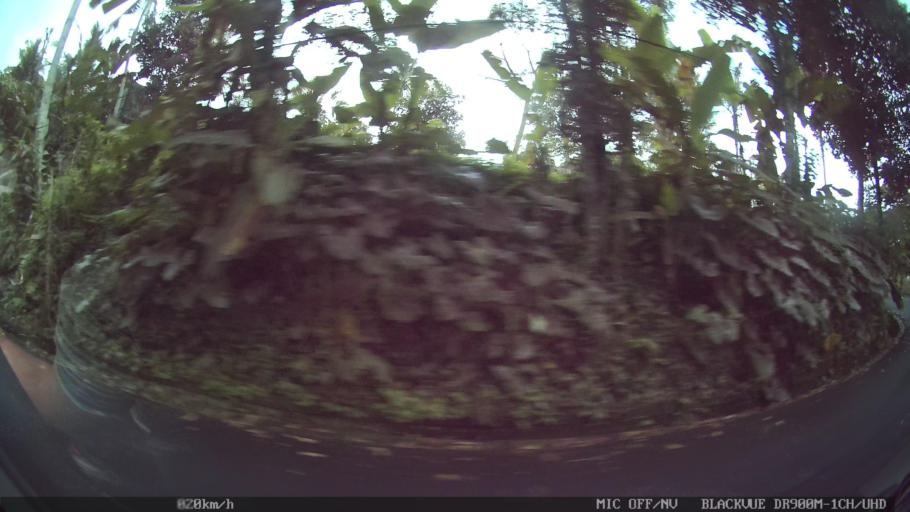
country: ID
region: Bali
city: Peneng
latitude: -8.3637
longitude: 115.1839
